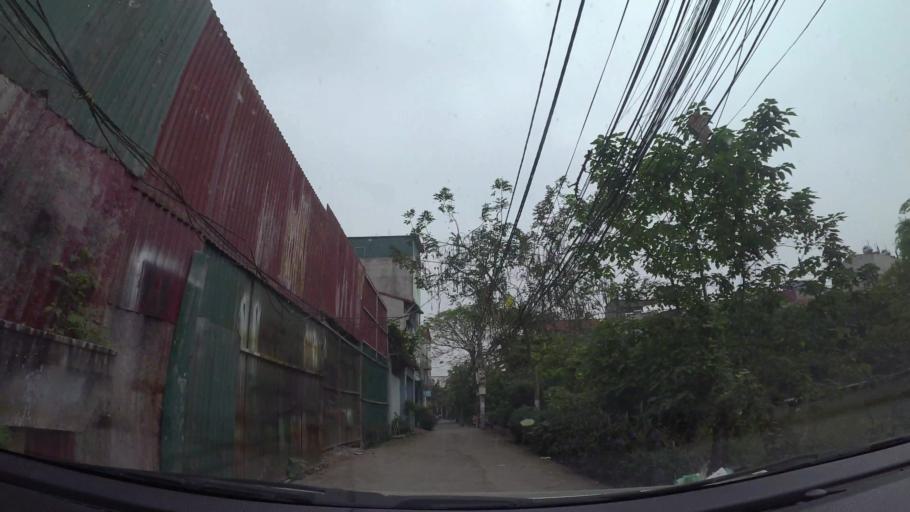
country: VN
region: Ha Noi
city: Tay Ho
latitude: 21.0655
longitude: 105.8326
